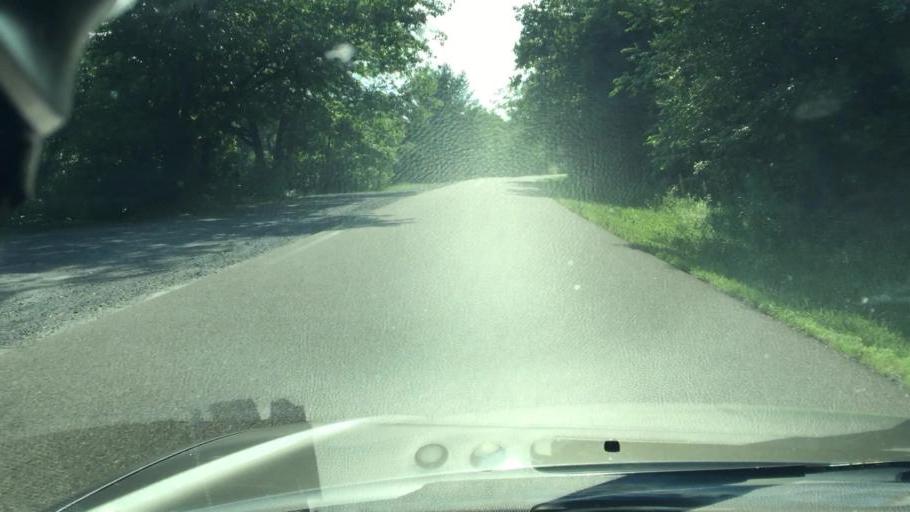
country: US
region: Pennsylvania
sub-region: Carbon County
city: Jim Thorpe
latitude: 40.8750
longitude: -75.7526
